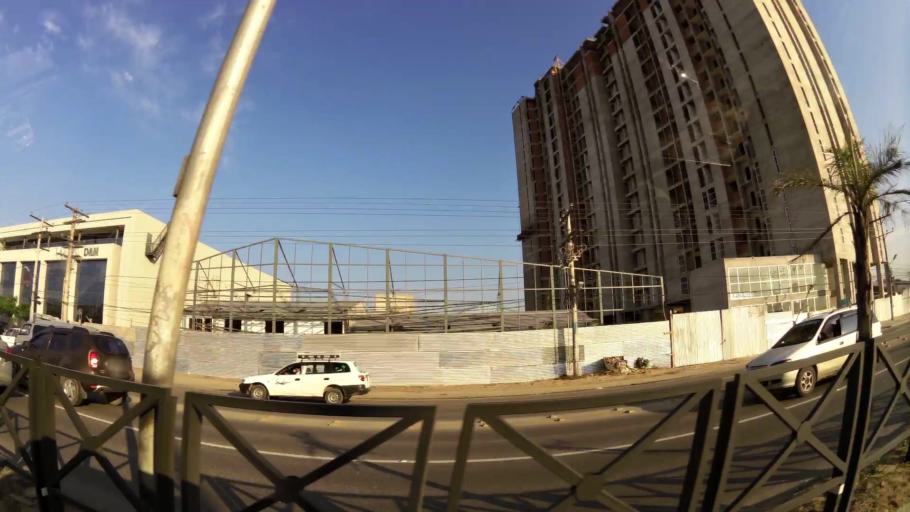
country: BO
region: Santa Cruz
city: Santa Cruz de la Sierra
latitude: -17.7267
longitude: -63.1663
